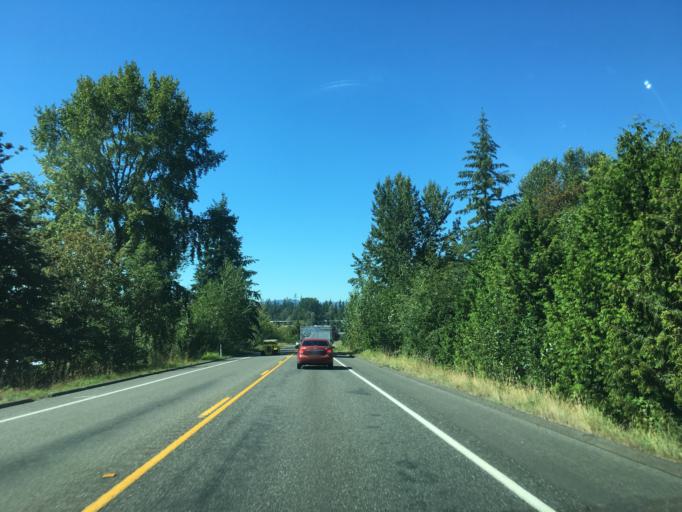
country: US
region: Washington
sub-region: Snohomish County
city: Arlington
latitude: 48.1762
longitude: -122.1271
